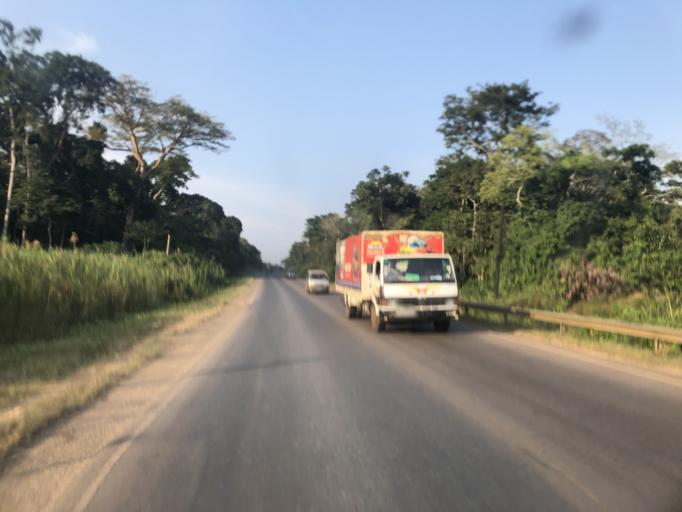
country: UG
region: Central Region
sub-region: Butambala District
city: Gombe
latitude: 0.1253
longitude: 32.1987
